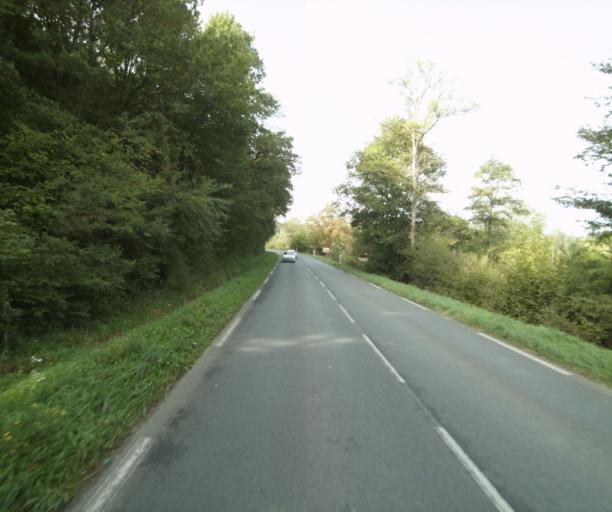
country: FR
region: Midi-Pyrenees
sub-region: Departement du Gers
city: Eauze
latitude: 43.8714
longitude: 0.1161
